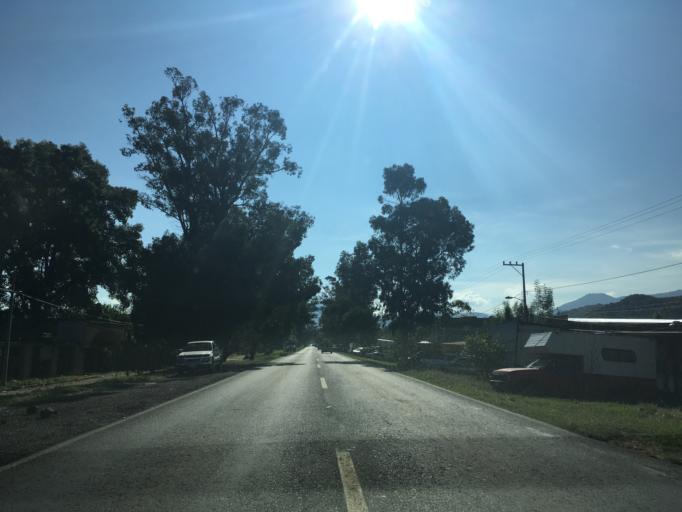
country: MX
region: Mexico
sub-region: Chalco
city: Chilchota
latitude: 19.8491
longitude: -102.1123
